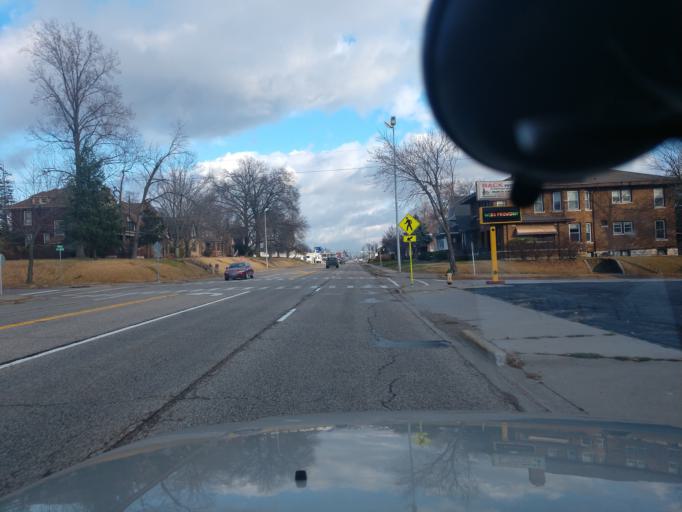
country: US
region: Illinois
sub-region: Adams County
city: Quincy
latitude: 39.9354
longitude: -91.3814
